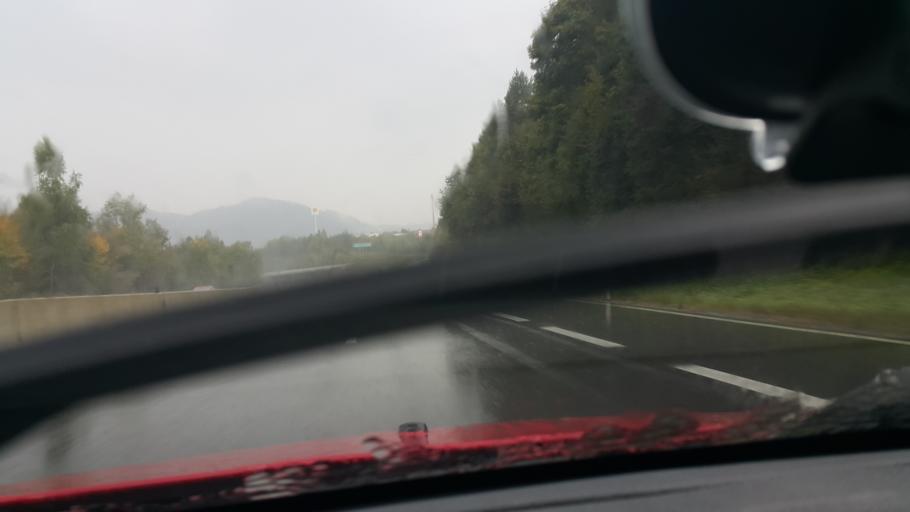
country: AT
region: Carinthia
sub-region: Politischer Bezirk Volkermarkt
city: Voelkermarkt
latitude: 46.6786
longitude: 14.6032
